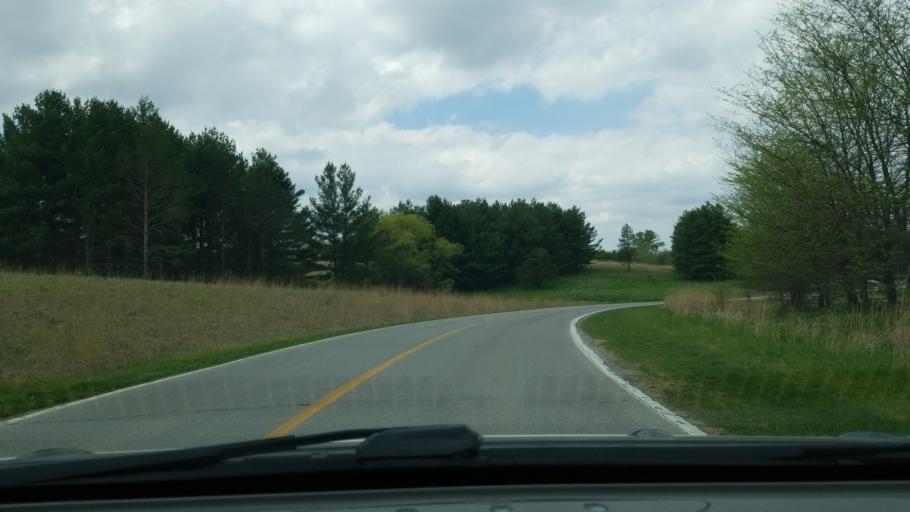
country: US
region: Nebraska
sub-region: Sarpy County
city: Chalco
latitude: 41.1681
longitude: -96.1594
